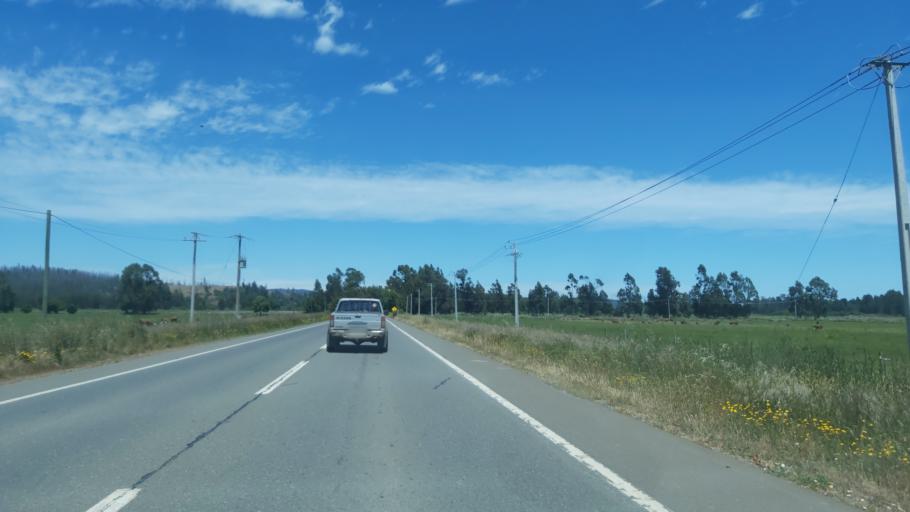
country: CL
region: Maule
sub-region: Provincia de Talca
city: Constitucion
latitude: -35.2960
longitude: -72.3696
